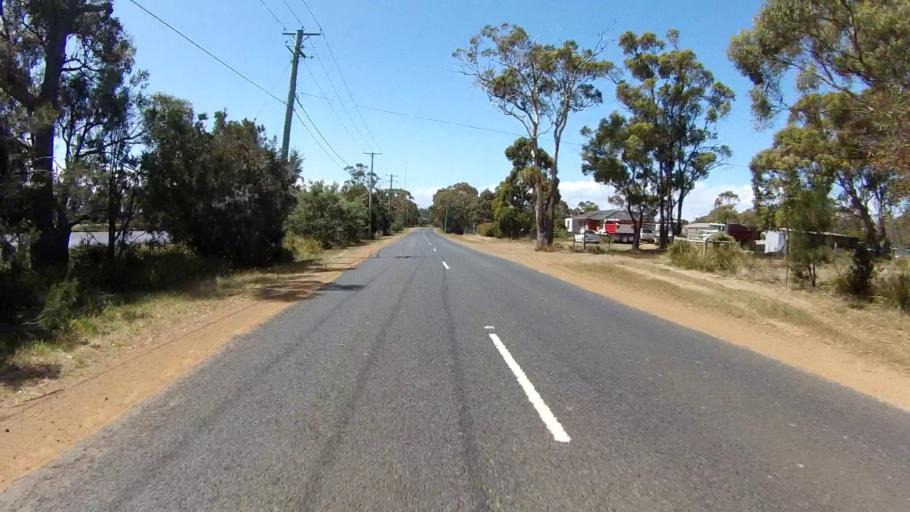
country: AU
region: Tasmania
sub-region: Clarence
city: Sandford
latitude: -42.9393
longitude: 147.4892
